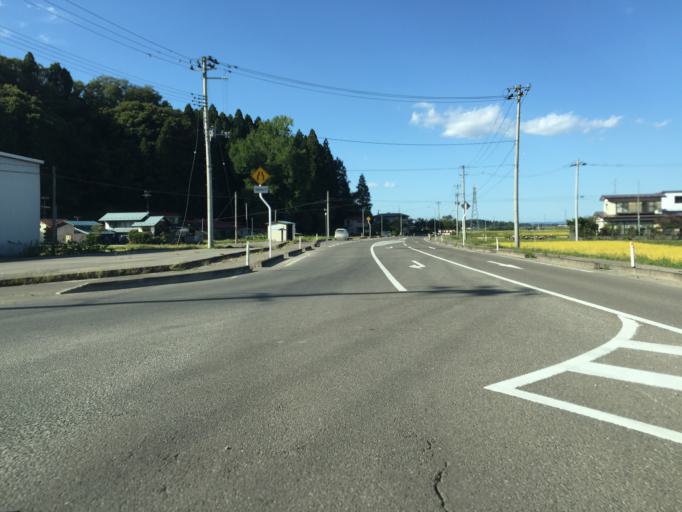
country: JP
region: Miyagi
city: Marumori
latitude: 37.8978
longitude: 140.7694
